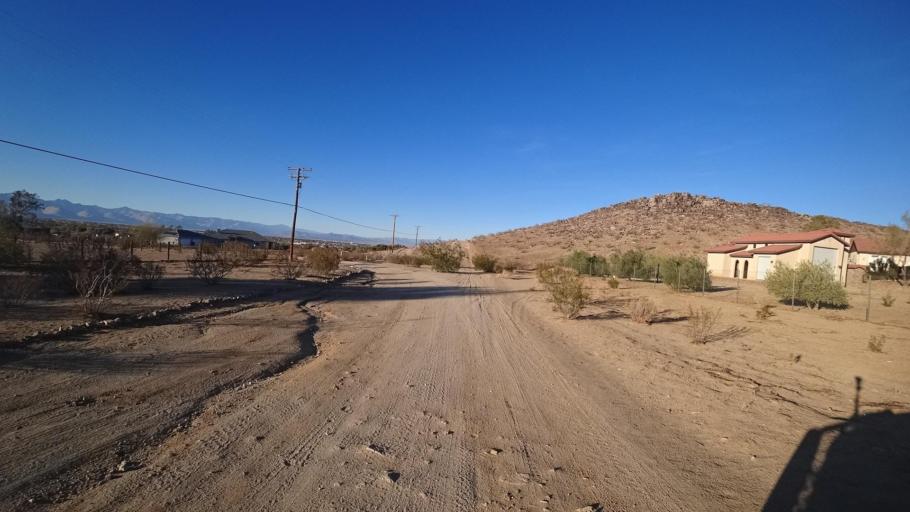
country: US
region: California
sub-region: Kern County
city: Ridgecrest
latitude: 35.5818
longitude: -117.6524
